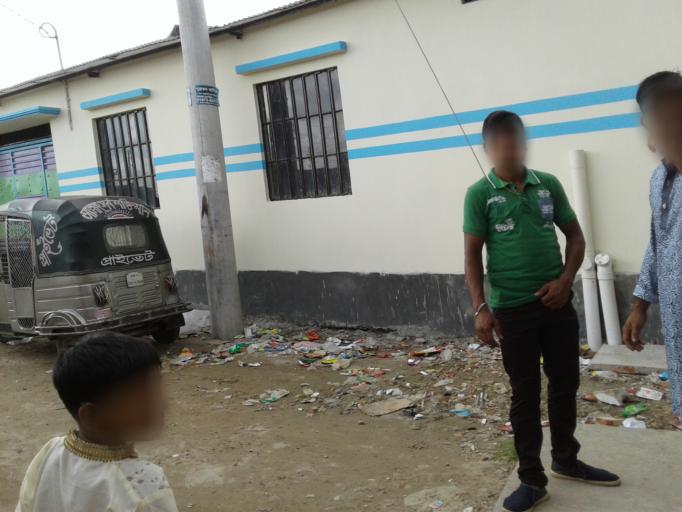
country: BD
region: Dhaka
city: Azimpur
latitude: 23.8103
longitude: 90.3817
